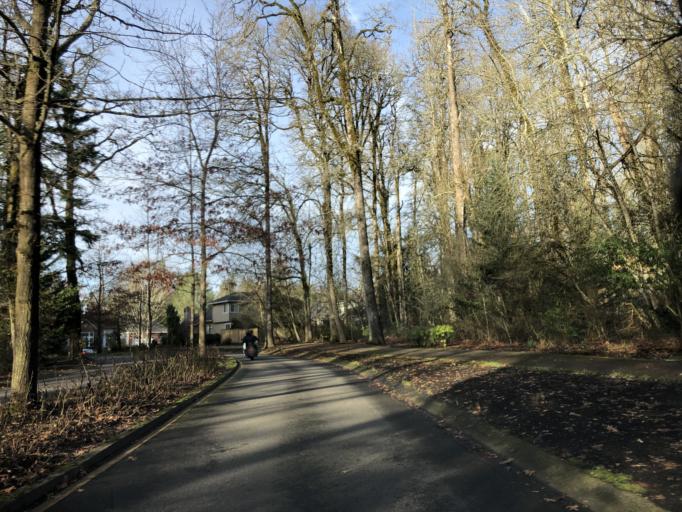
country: US
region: Oregon
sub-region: Washington County
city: Durham
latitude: 45.4219
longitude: -122.7328
